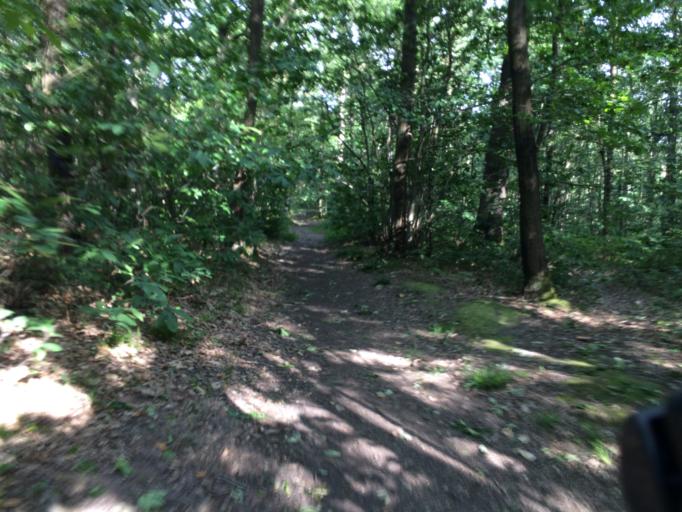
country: FR
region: Ile-de-France
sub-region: Departement de l'Essonne
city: Igny
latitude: 48.7548
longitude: 2.2342
